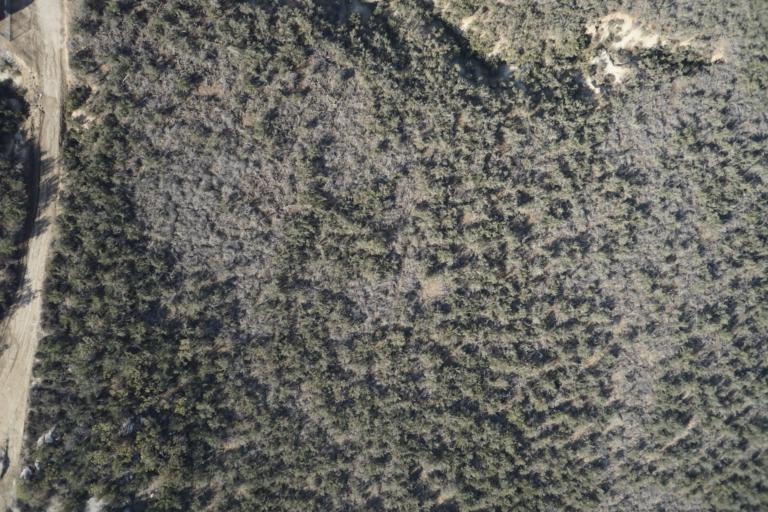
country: US
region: California
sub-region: Riverside County
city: Valle Vista
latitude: 33.6308
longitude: -116.8928
